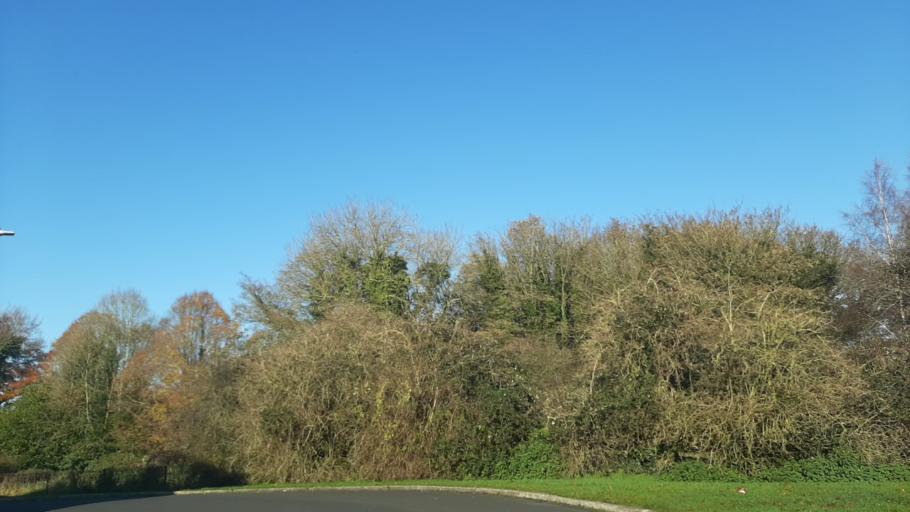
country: IE
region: Leinster
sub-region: Kildare
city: Rathangan
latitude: 53.2194
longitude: -6.9962
